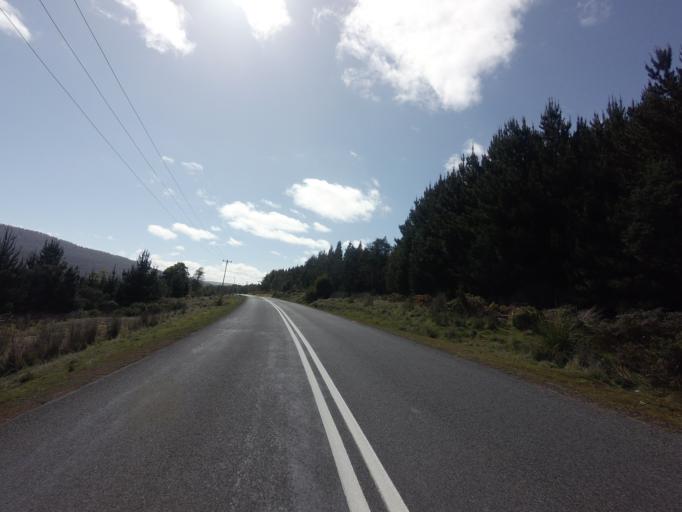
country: AU
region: Tasmania
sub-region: Derwent Valley
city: New Norfolk
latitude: -42.7435
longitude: 146.6563
